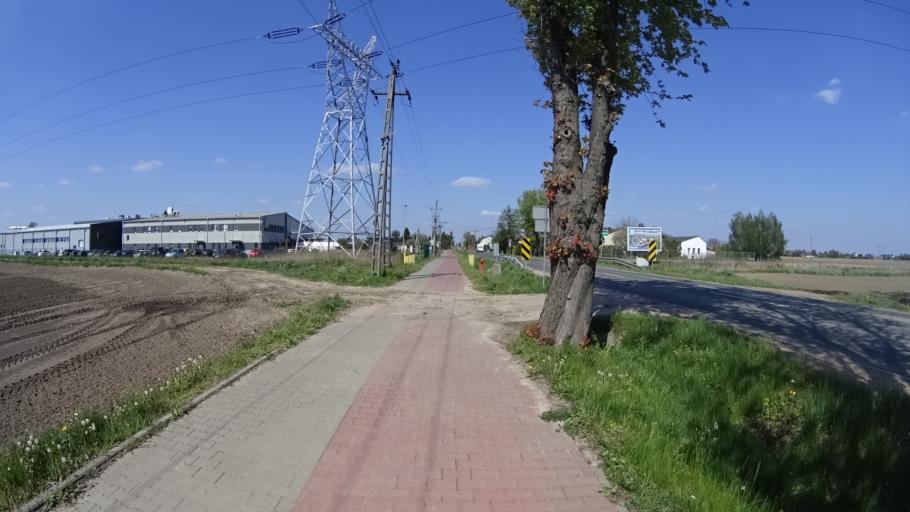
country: PL
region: Masovian Voivodeship
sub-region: Powiat warszawski zachodni
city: Stare Babice
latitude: 52.2387
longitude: 20.8172
